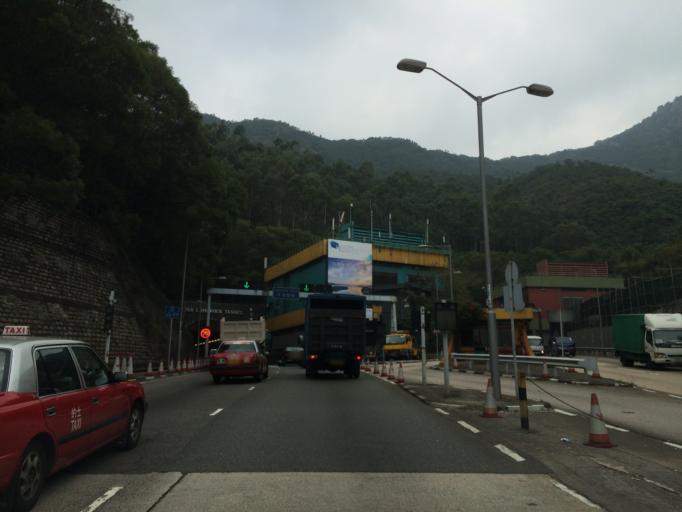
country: HK
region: Wong Tai Sin
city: Wong Tai Sin
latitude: 22.3454
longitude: 114.1814
